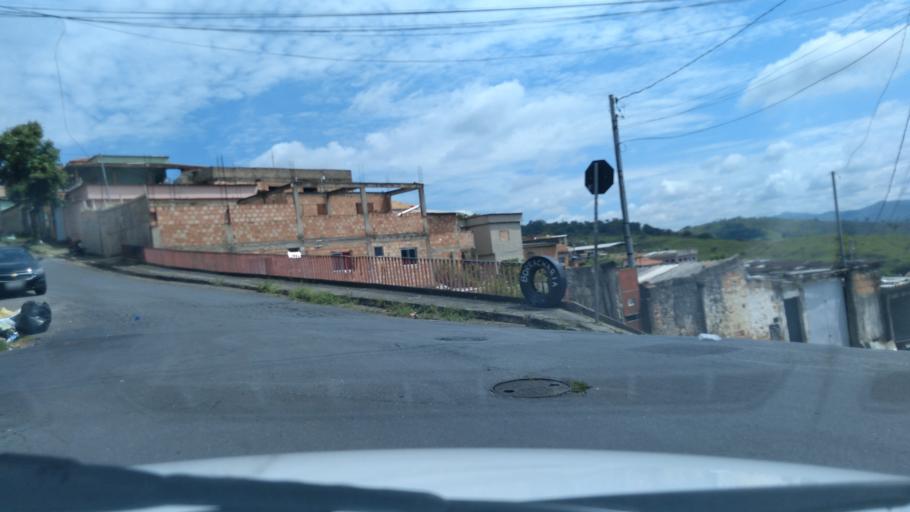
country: BR
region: Minas Gerais
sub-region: Belo Horizonte
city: Belo Horizonte
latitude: -19.9016
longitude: -43.8888
